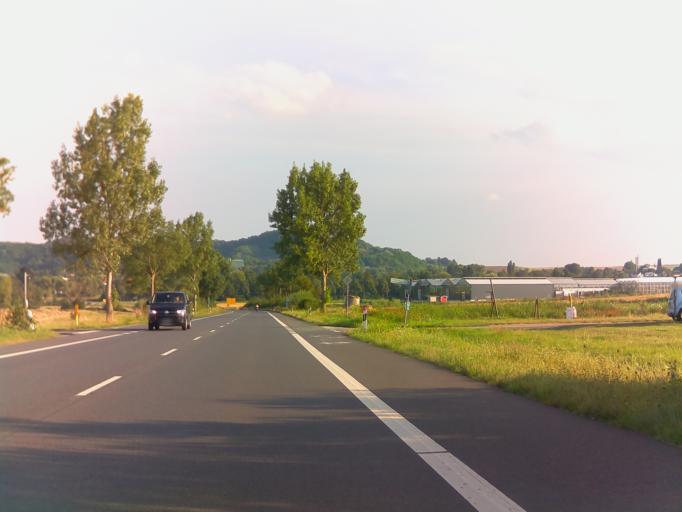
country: DE
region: Hesse
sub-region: Regierungsbezirk Darmstadt
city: Rossdorf
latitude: 49.8685
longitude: 8.7657
